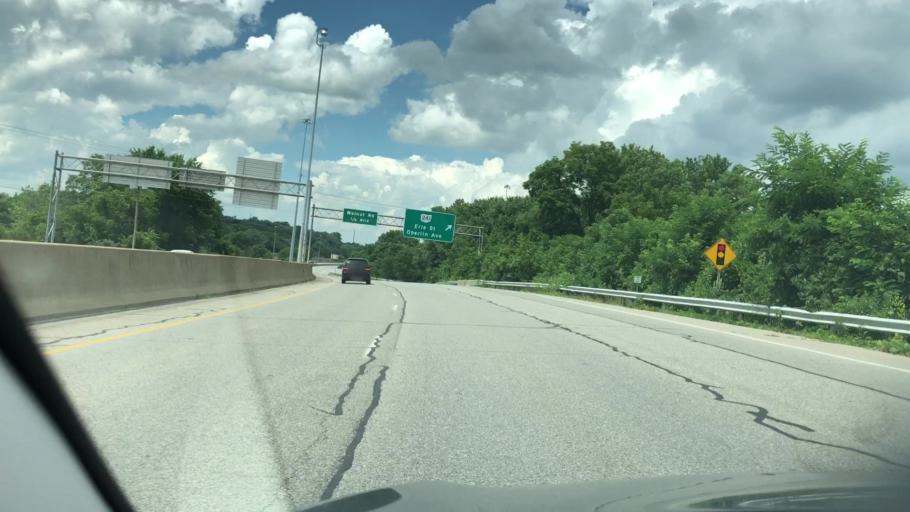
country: US
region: Ohio
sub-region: Stark County
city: Massillon
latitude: 40.7833
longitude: -81.5177
